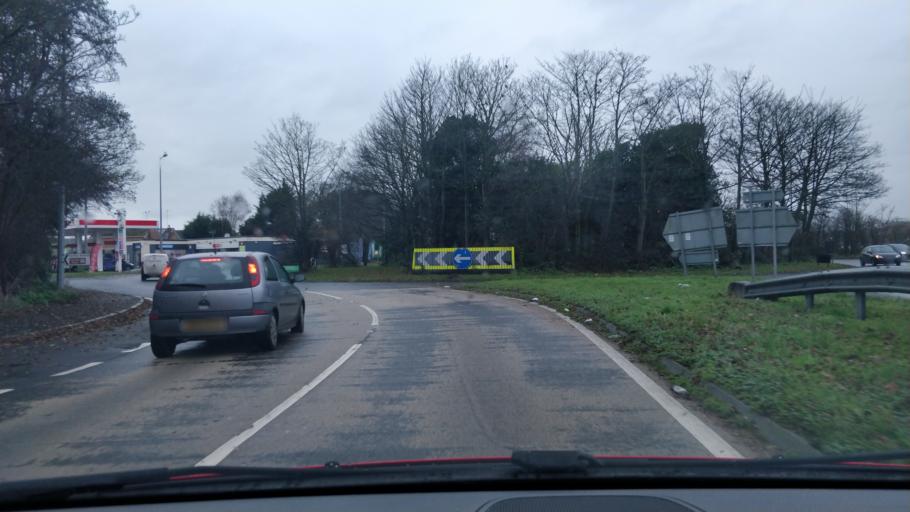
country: GB
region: England
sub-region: Sefton
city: Formby
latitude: 53.5680
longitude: -3.0474
